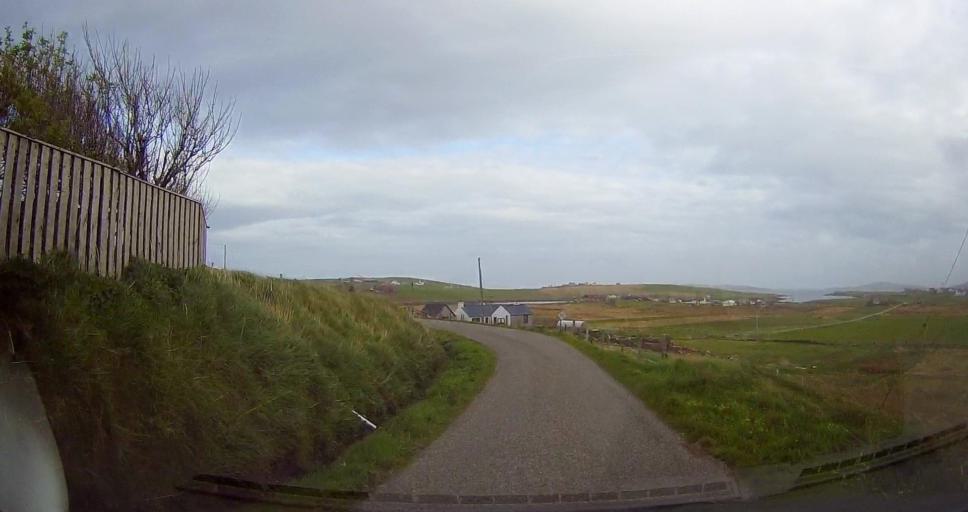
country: GB
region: Scotland
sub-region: Shetland Islands
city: Sandwick
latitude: 60.0486
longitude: -1.2172
